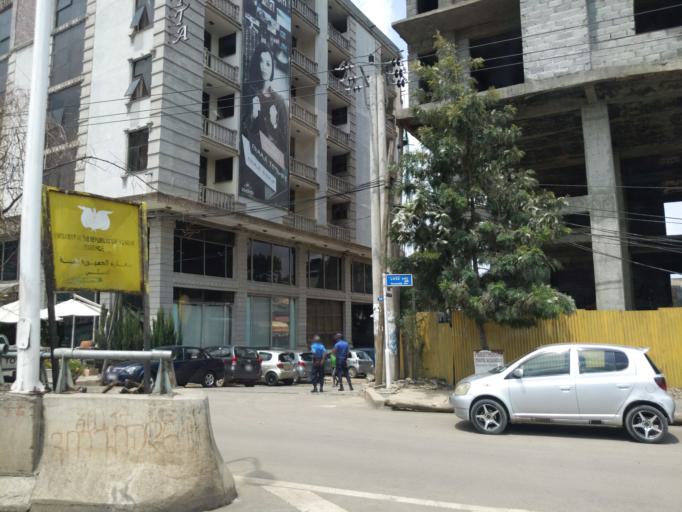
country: ET
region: Adis Abeba
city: Addis Ababa
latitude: 8.9903
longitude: 38.7786
